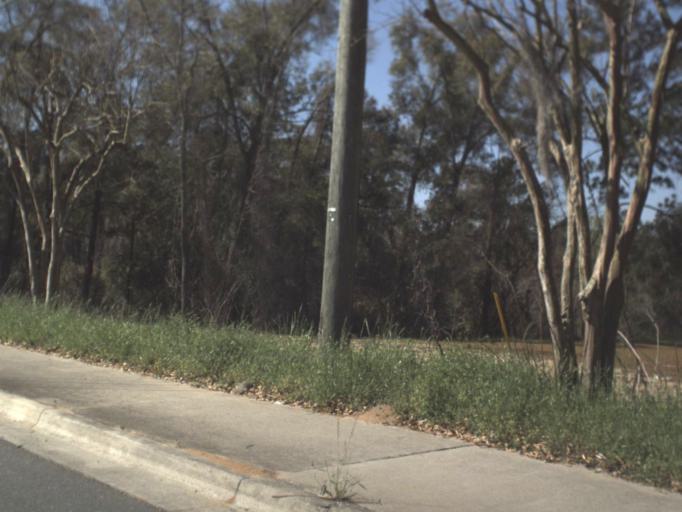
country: US
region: Florida
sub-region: Leon County
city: Tallahassee
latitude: 30.4062
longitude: -84.2840
